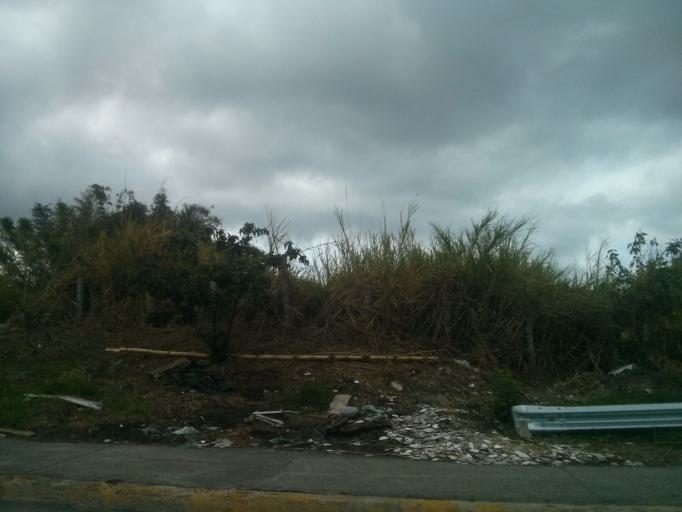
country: CR
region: San Jose
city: San Pedro
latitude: 9.9159
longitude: -84.0673
